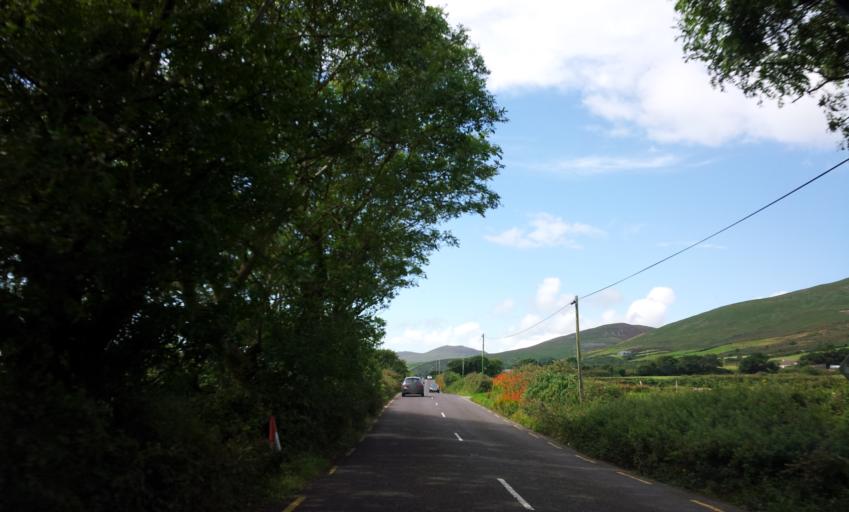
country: IE
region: Munster
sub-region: Ciarrai
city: Killorglin
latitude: 52.1478
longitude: -9.9370
